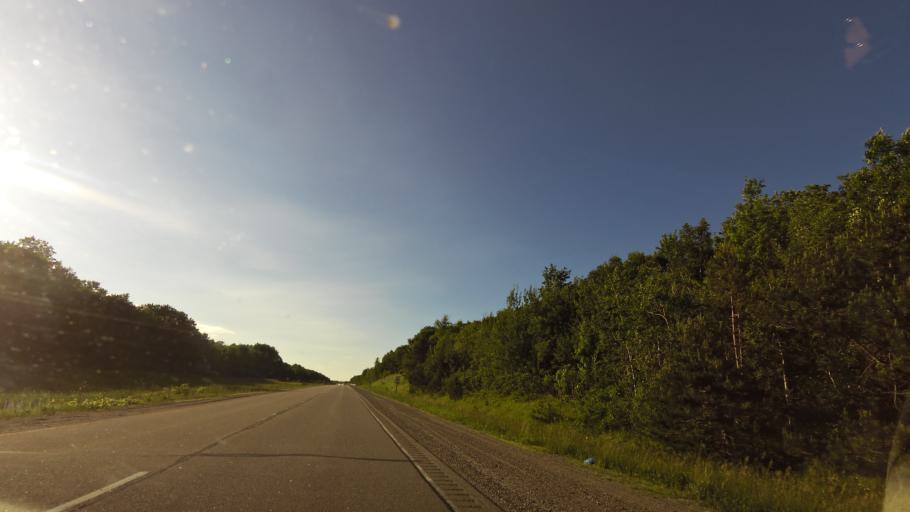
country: CA
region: Ontario
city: Midland
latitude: 44.7160
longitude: -79.6691
